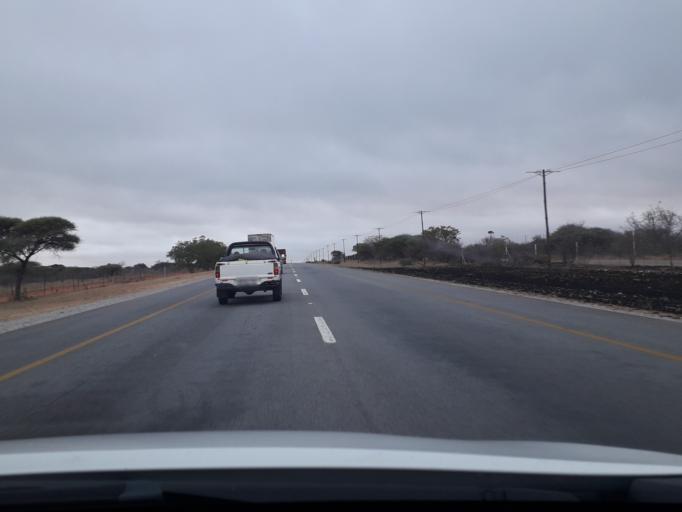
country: ZA
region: Limpopo
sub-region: Capricorn District Municipality
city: Mankoeng
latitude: -23.5873
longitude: 29.6644
